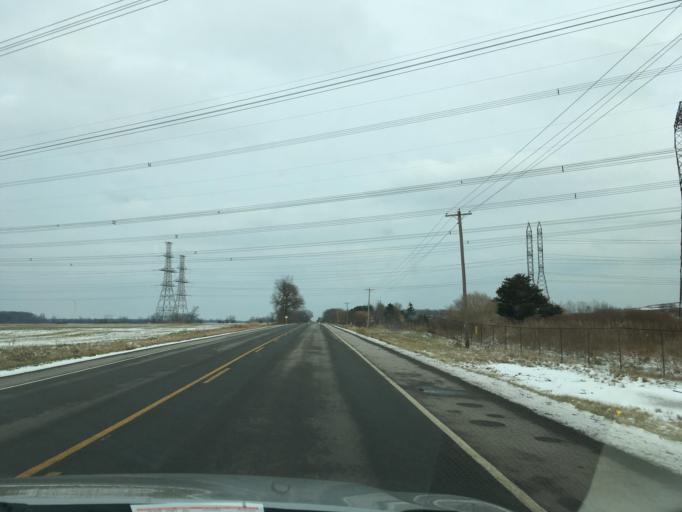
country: CA
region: Ontario
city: Norfolk County
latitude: 42.8138
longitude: -80.0542
